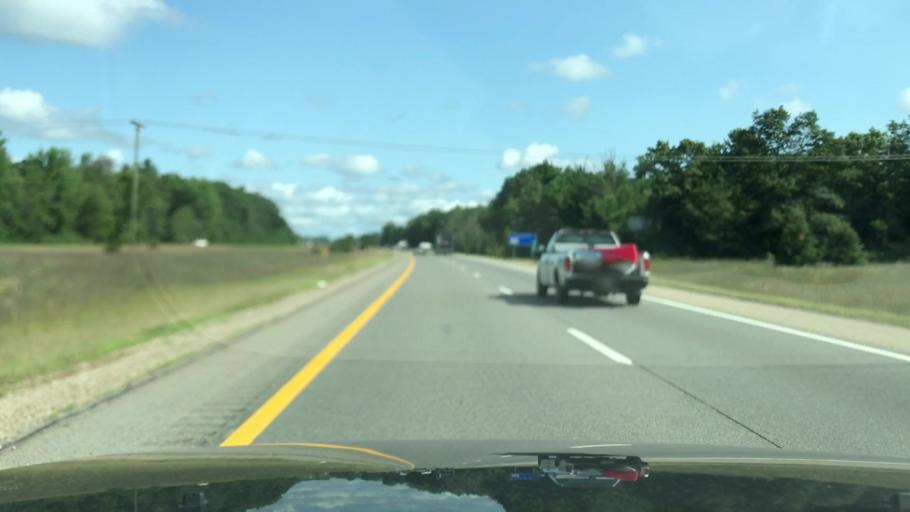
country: US
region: Michigan
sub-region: Kent County
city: Cedar Springs
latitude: 43.2775
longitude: -85.5408
